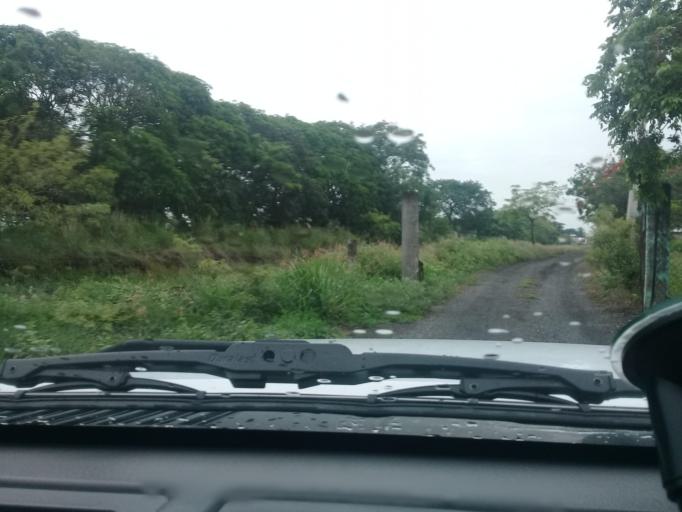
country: MX
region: Veracruz
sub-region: Puente Nacional
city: Cabezas
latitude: 19.3634
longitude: -96.4038
